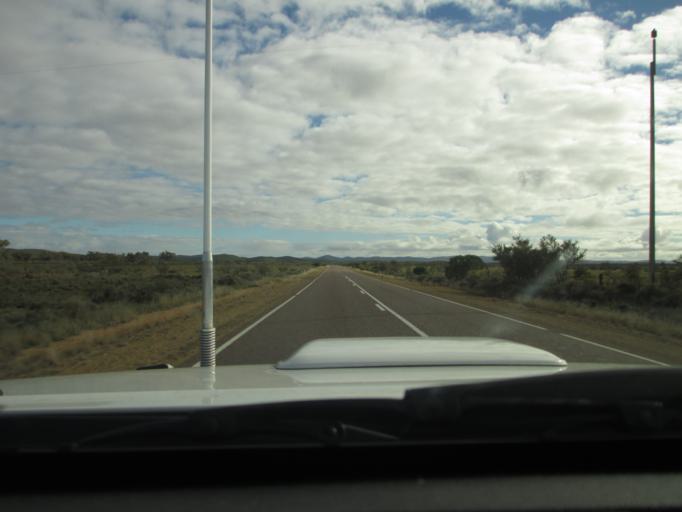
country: AU
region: South Australia
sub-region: Flinders Ranges
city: Quorn
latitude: -32.3467
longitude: 138.4863
